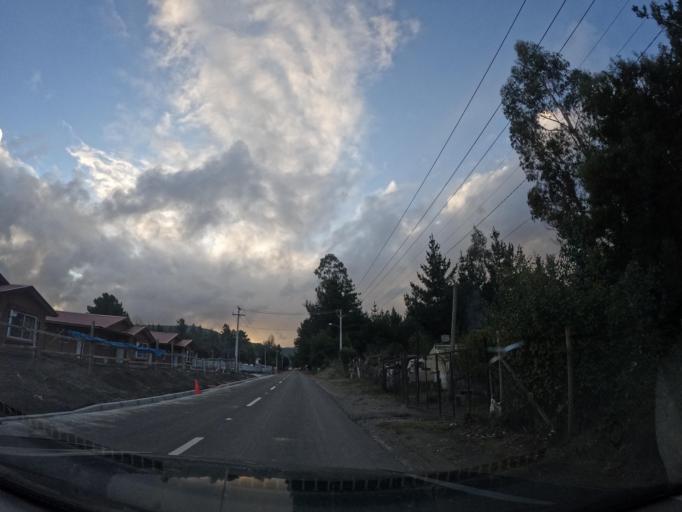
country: CL
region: Biobio
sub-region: Provincia de Concepcion
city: Chiguayante
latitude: -37.0576
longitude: -72.9554
